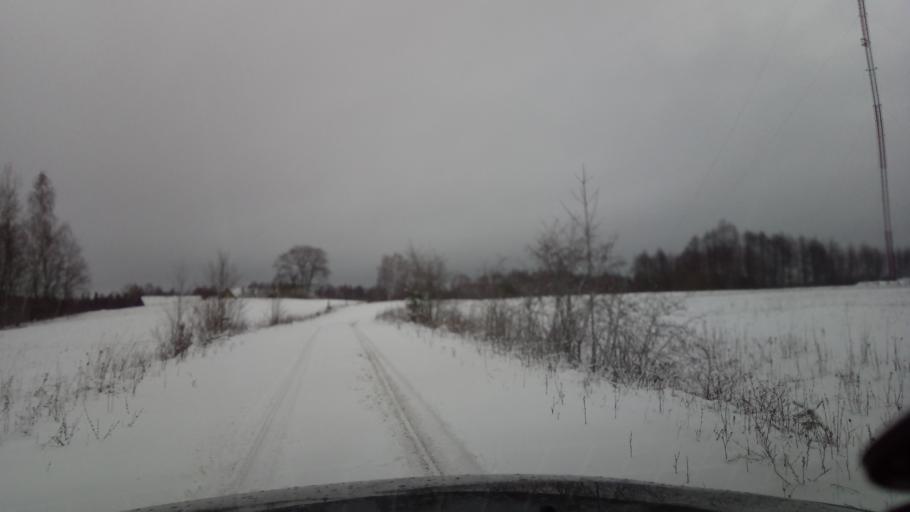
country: LT
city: Zarasai
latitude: 55.6199
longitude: 25.9447
